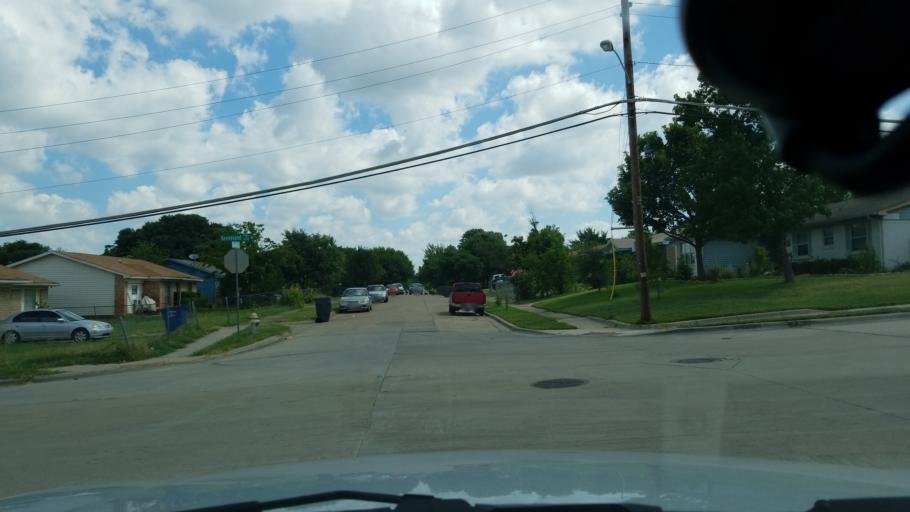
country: US
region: Texas
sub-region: Dallas County
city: Cockrell Hill
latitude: 32.7369
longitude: -96.9292
